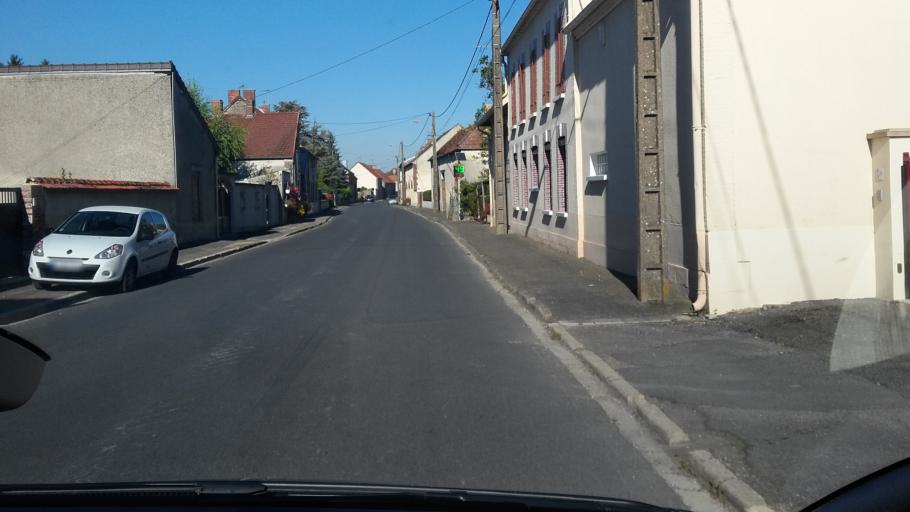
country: FR
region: Champagne-Ardenne
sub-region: Departement de la Marne
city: Vertus
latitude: 48.8420
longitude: 3.9606
